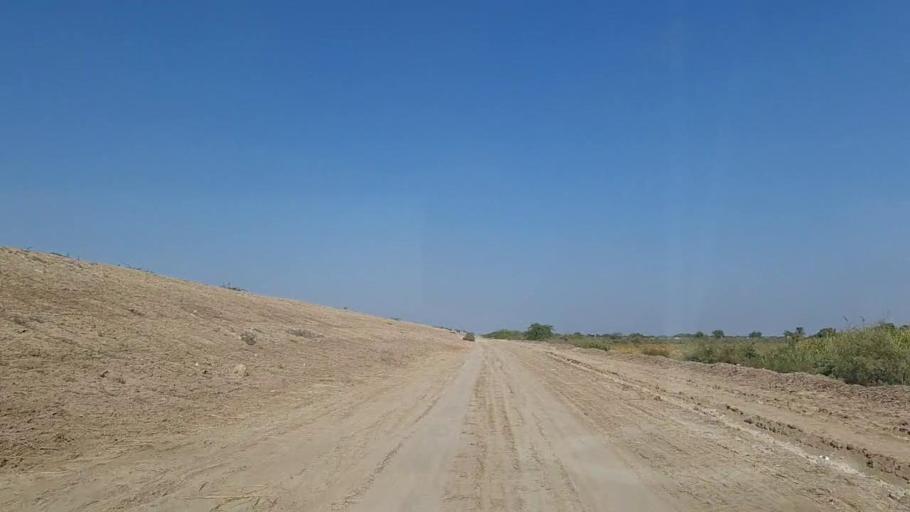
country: PK
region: Sindh
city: Chuhar Jamali
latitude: 24.4688
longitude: 68.0065
